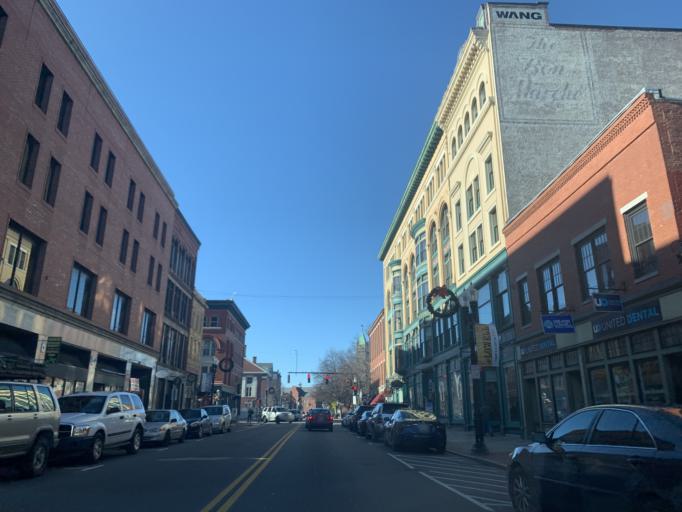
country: US
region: Massachusetts
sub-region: Middlesex County
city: Lowell
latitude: 42.6457
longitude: -71.3098
